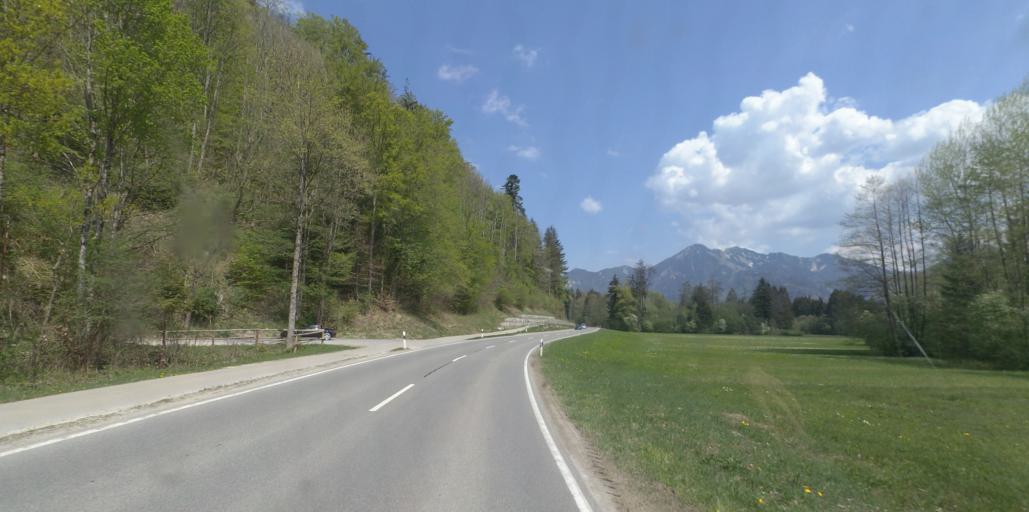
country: DE
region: Bavaria
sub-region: Upper Bavaria
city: Schleching
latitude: 47.7352
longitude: 12.4189
